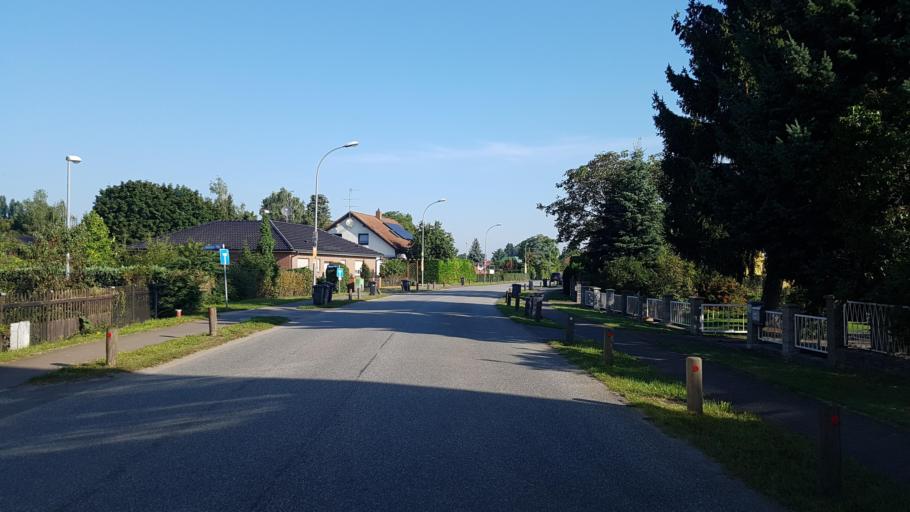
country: DE
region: Brandenburg
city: Brandenburg an der Havel
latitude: 52.4254
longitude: 12.5757
